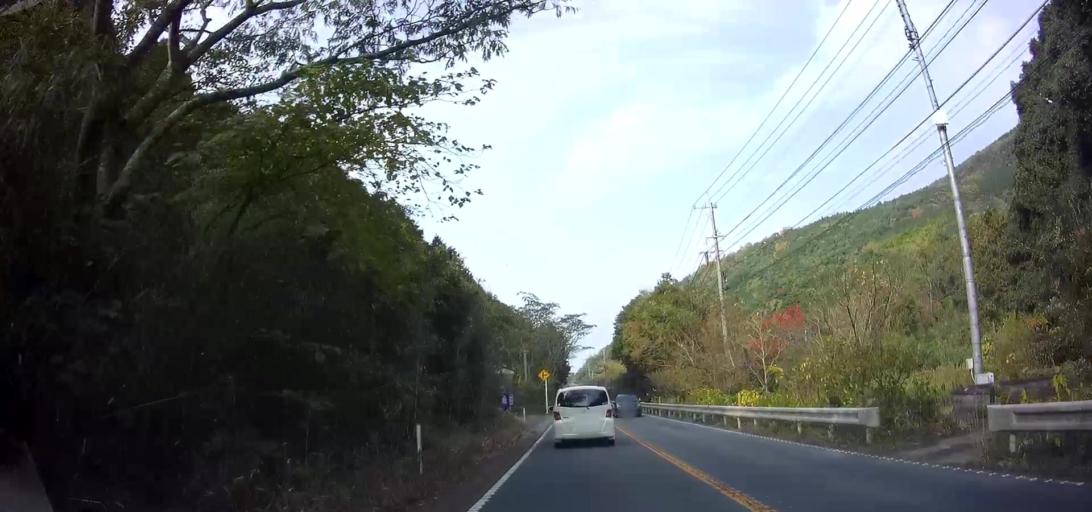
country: JP
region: Nagasaki
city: Shimabara
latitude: 32.7614
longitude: 130.2080
